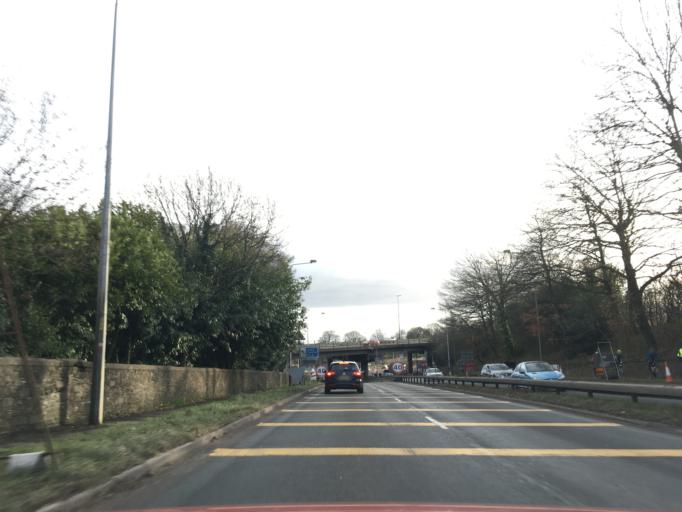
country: GB
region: Wales
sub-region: Newport
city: Newport
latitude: 51.5681
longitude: -3.0367
